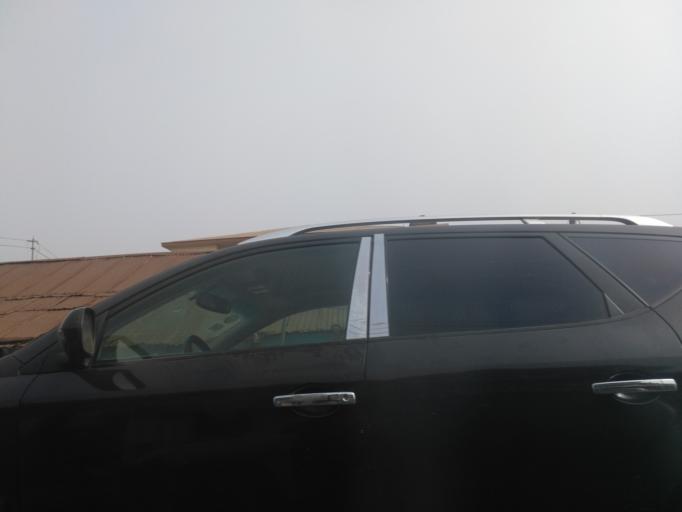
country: GH
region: Ashanti
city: Kumasi
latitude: 6.7035
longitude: -1.6208
